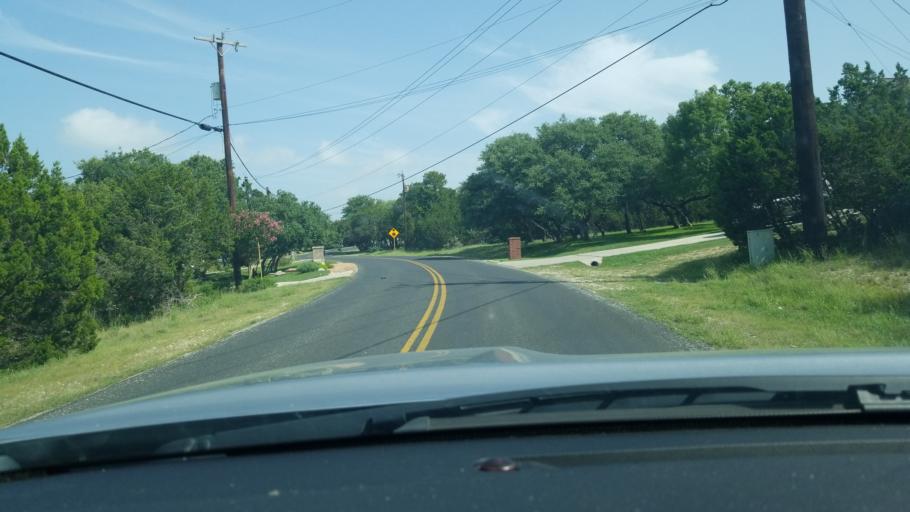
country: US
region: Texas
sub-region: Bexar County
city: Timberwood Park
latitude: 29.7022
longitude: -98.4898
